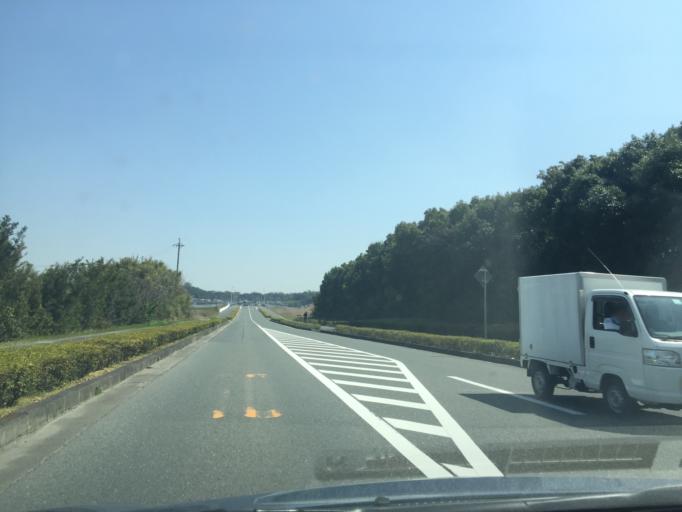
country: JP
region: Shizuoka
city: Hamamatsu
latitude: 34.7970
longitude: 137.6420
